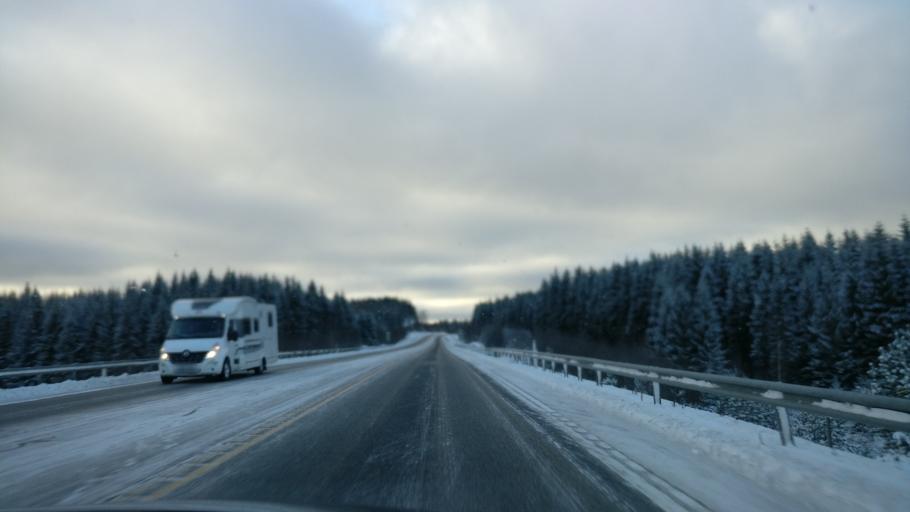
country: FI
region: Southern Savonia
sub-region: Mikkeli
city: Pertunmaa
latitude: 61.3915
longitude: 26.3662
